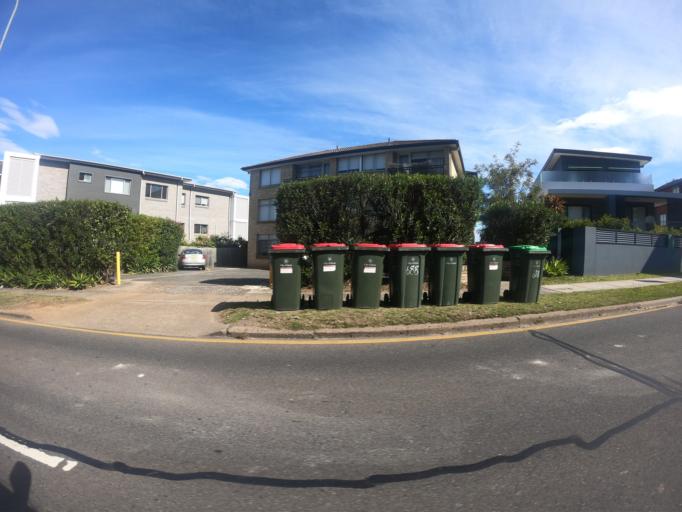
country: AU
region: New South Wales
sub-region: Canada Bay
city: Rhodes
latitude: -33.8166
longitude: 151.1074
